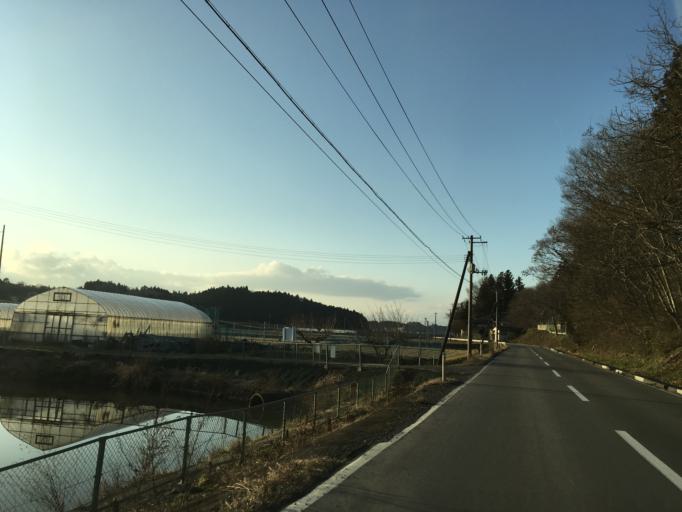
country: JP
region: Iwate
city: Ichinoseki
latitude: 38.8074
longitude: 141.2190
